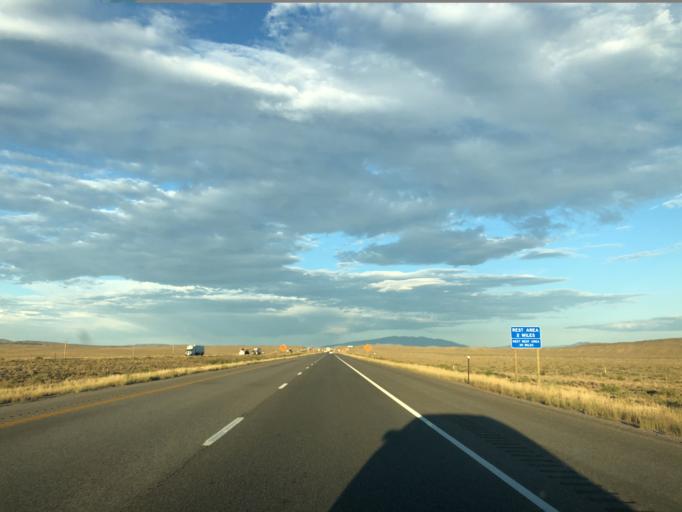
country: US
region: Wyoming
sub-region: Carbon County
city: Rawlins
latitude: 41.7606
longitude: -106.9989
